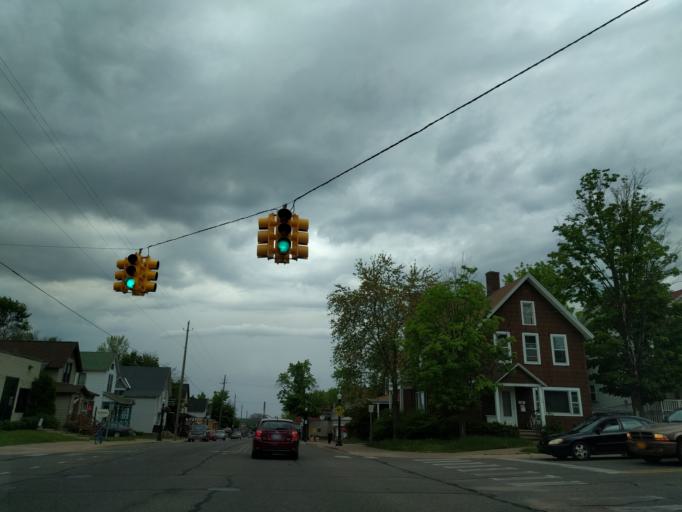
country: US
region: Michigan
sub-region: Marquette County
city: Marquette
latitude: 46.5491
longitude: -87.3947
